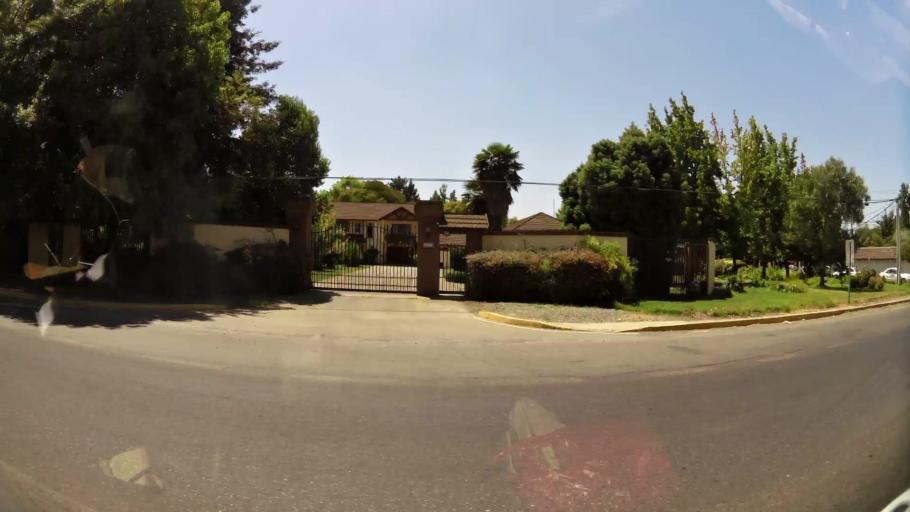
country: CL
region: Maule
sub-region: Provincia de Talca
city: Talca
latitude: -35.4362
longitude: -71.6234
